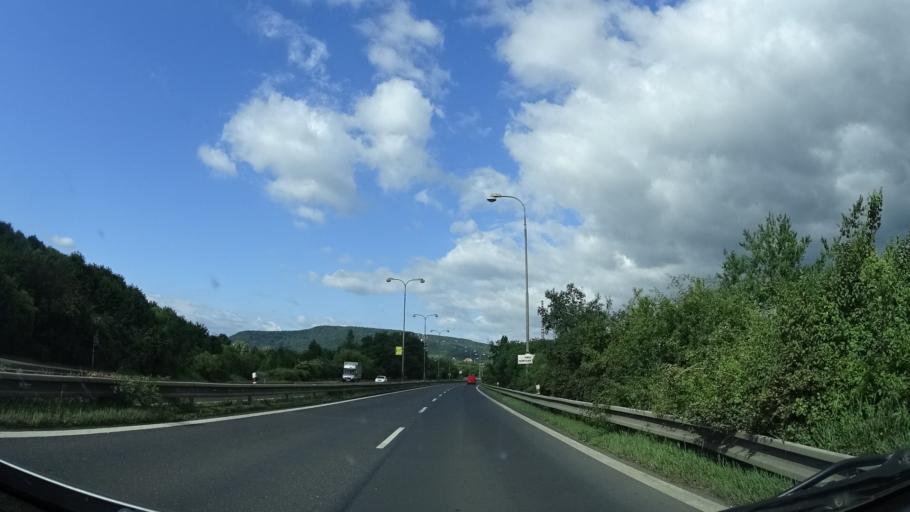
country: CZ
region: Ustecky
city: Trmice
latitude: 50.6496
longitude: 14.0120
